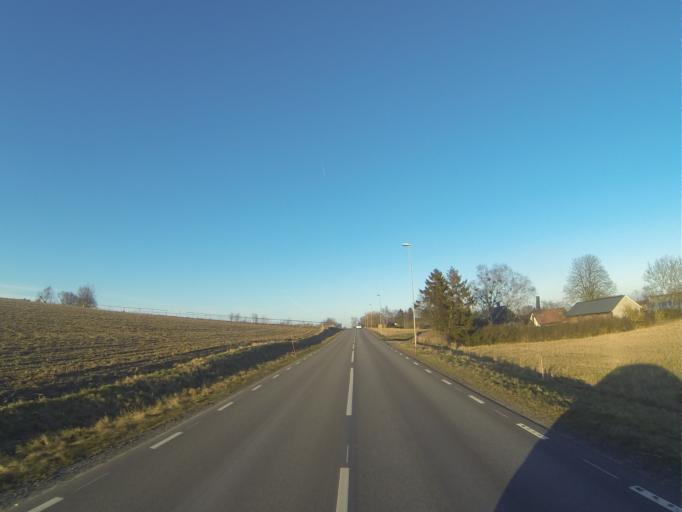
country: SE
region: Skane
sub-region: Malmo
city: Oxie
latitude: 55.5643
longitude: 13.1113
